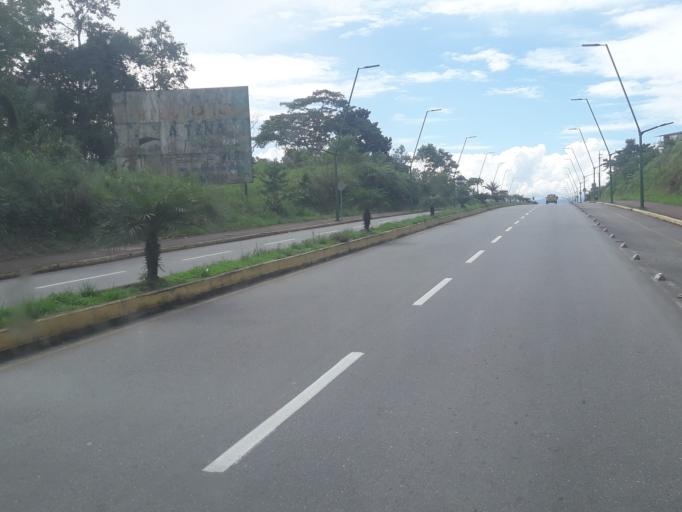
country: EC
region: Napo
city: Tena
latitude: -1.0208
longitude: -77.8060
